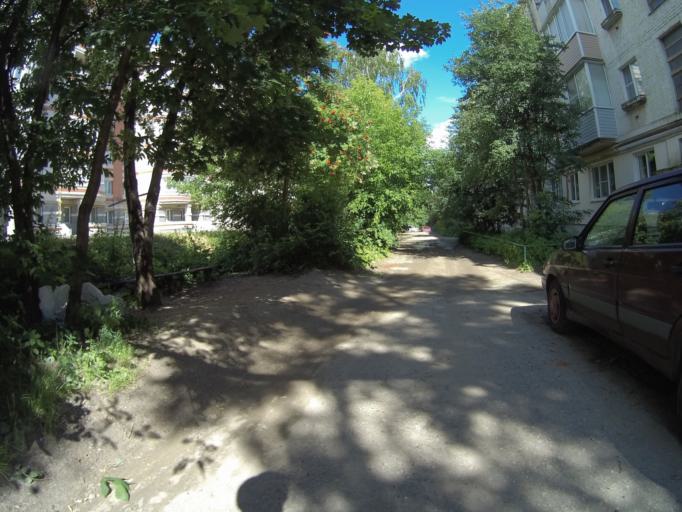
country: RU
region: Vladimir
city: Vladimir
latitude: 56.1374
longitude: 40.4164
